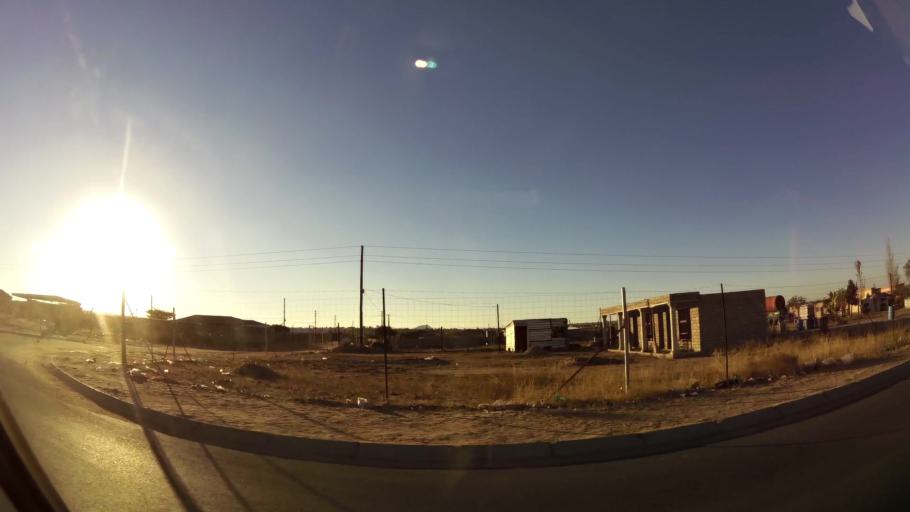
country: ZA
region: Limpopo
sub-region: Capricorn District Municipality
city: Polokwane
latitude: -23.8364
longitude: 29.3606
